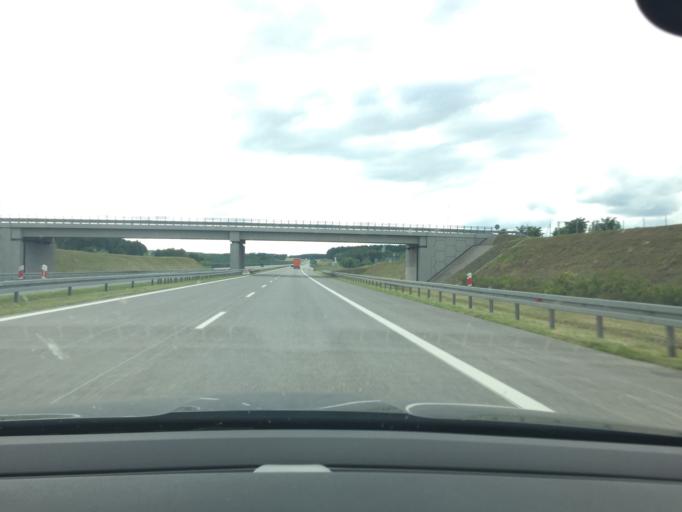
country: PL
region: Lubusz
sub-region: Powiat swiebodzinski
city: Lubrza
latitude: 52.3170
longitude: 15.4383
